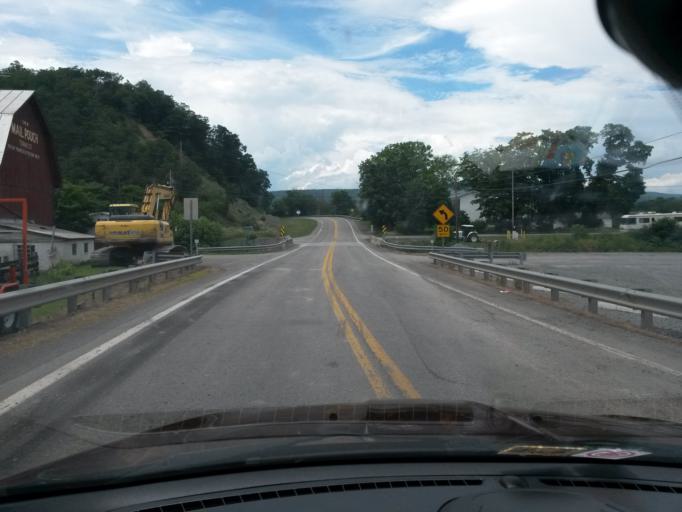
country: US
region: West Virginia
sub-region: Grant County
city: Petersburg
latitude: 38.9925
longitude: -79.0443
